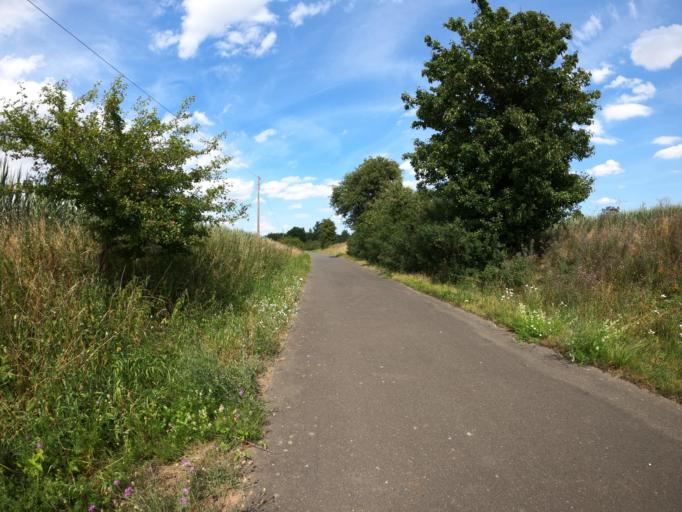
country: DE
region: Mecklenburg-Vorpommern
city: Woldegk
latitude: 53.3404
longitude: 13.5989
